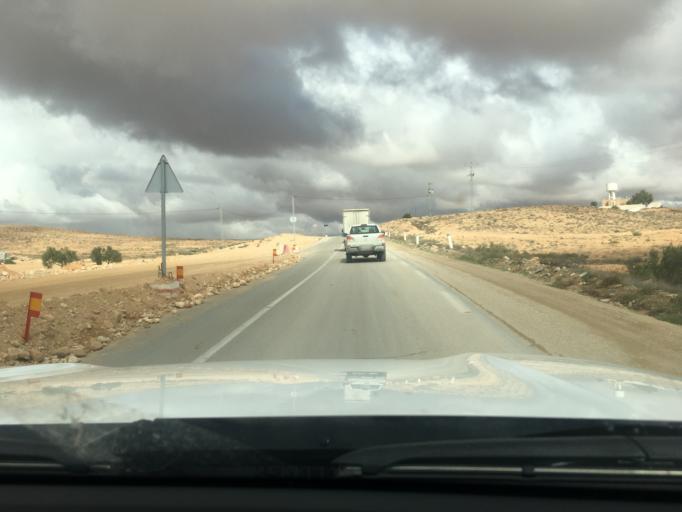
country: TN
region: Tataouine
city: Tataouine
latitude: 33.0759
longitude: 10.4913
